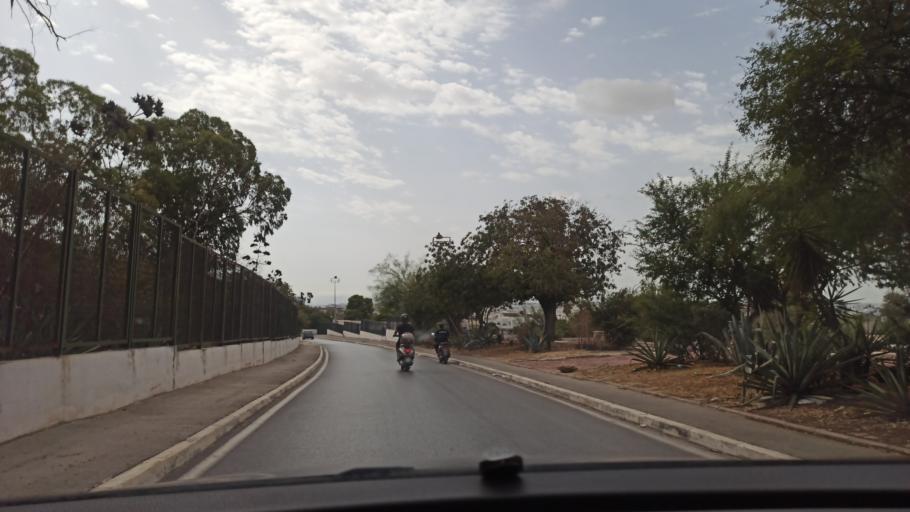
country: TN
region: Tunis
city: Tunis
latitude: 36.8221
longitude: 10.1672
